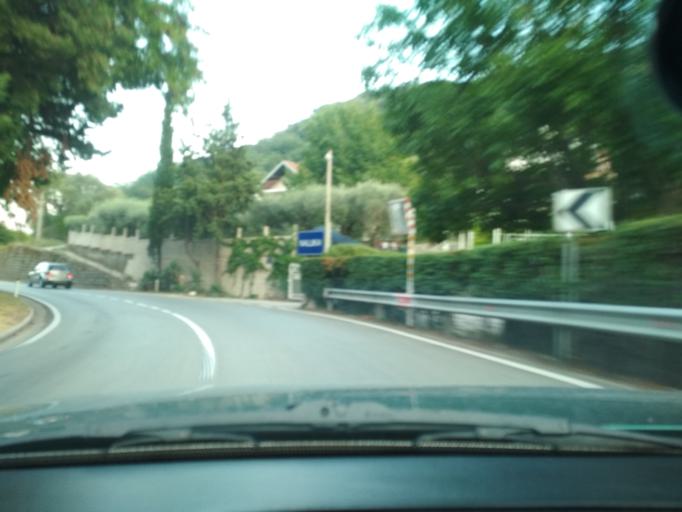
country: ME
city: Lipci
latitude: 42.4870
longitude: 18.6519
